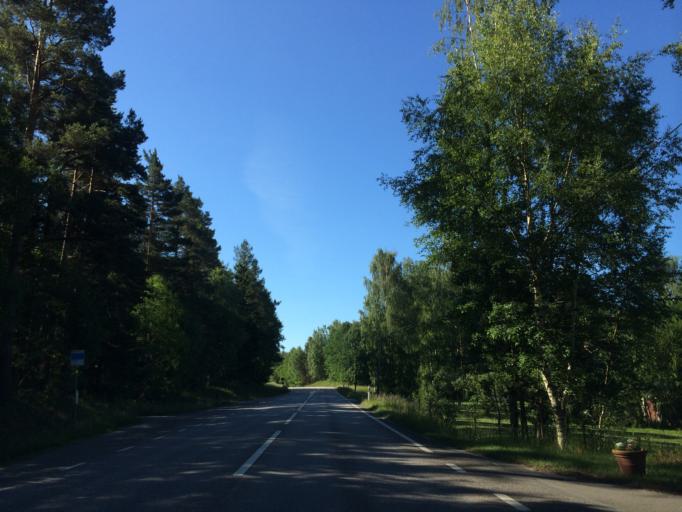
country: SE
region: OEstergoetland
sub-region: Motala Kommun
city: Ryd
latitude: 58.7032
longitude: 14.9639
